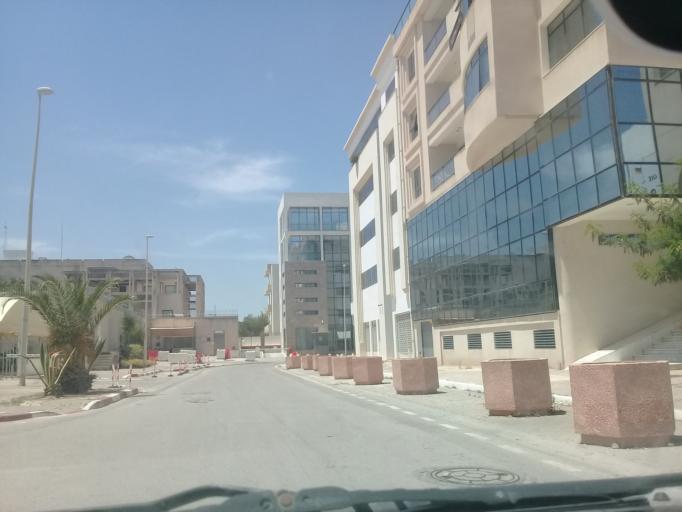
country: TN
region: Ariana
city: Ariana
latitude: 36.8339
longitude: 10.2423
